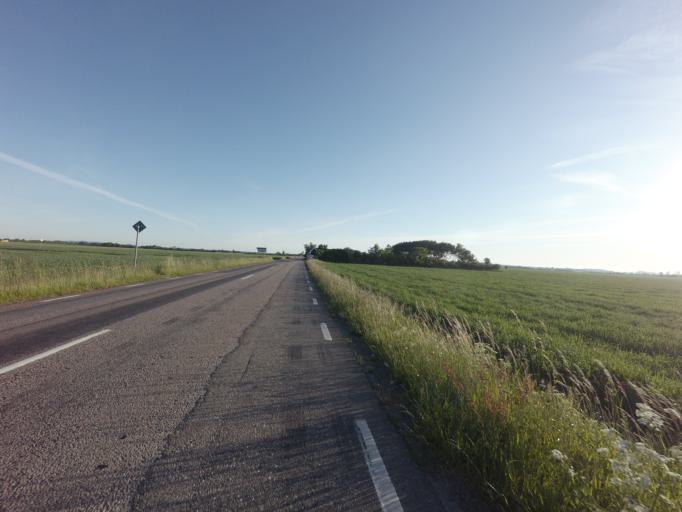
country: SE
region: Skane
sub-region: Helsingborg
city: Odakra
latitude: 56.1825
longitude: 12.6764
